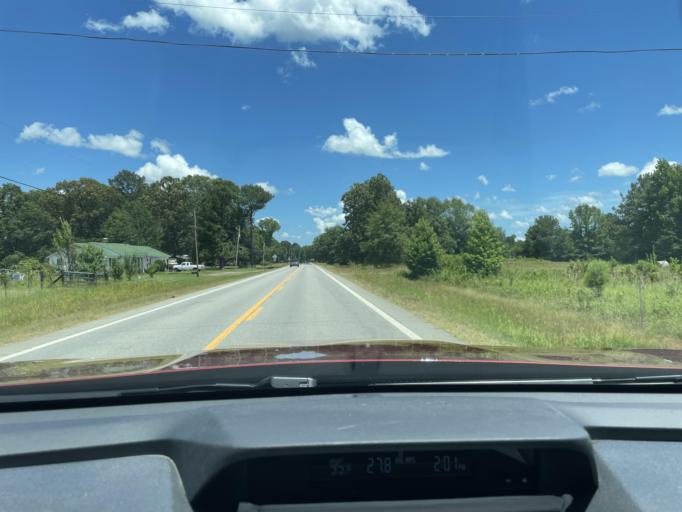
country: US
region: Arkansas
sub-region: Drew County
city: Monticello
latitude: 33.6047
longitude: -91.7321
